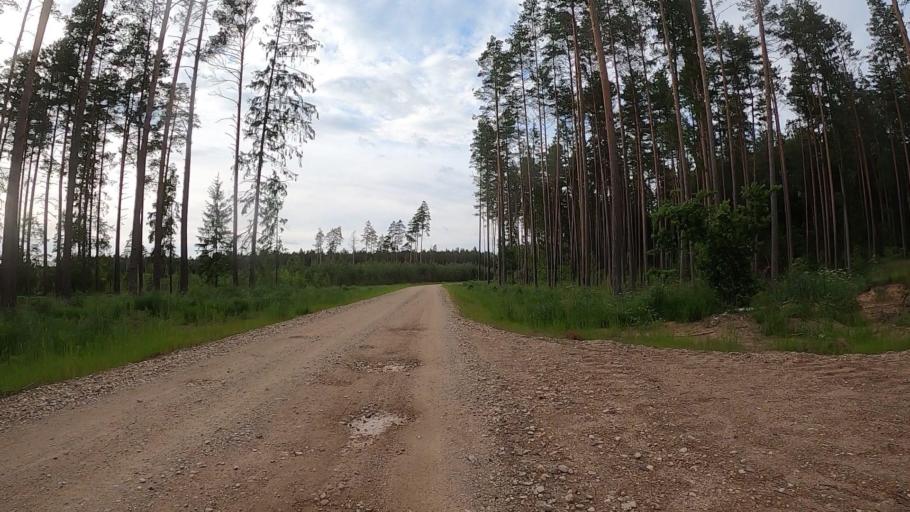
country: LV
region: Olaine
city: Olaine
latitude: 56.7679
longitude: 23.9034
